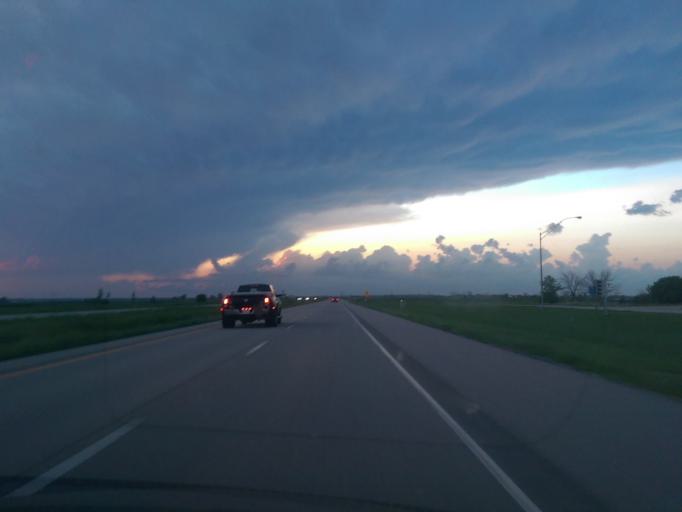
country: US
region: Nebraska
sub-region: Otoe County
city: Nebraska City
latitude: 40.7067
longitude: -95.7954
